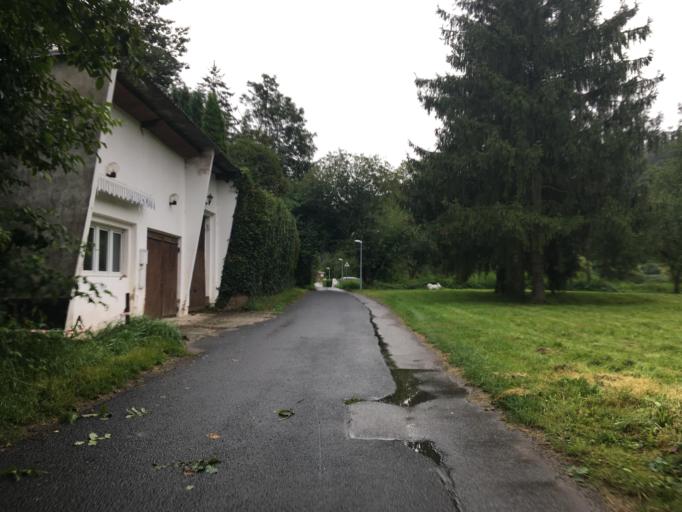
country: DE
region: Saxony
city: Struppen
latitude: 50.9460
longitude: 14.0058
